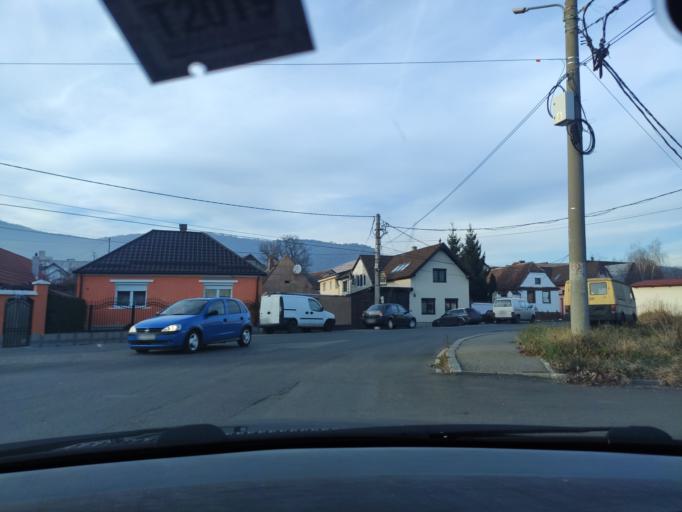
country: RO
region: Brasov
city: Codlea
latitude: 45.7029
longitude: 25.4522
